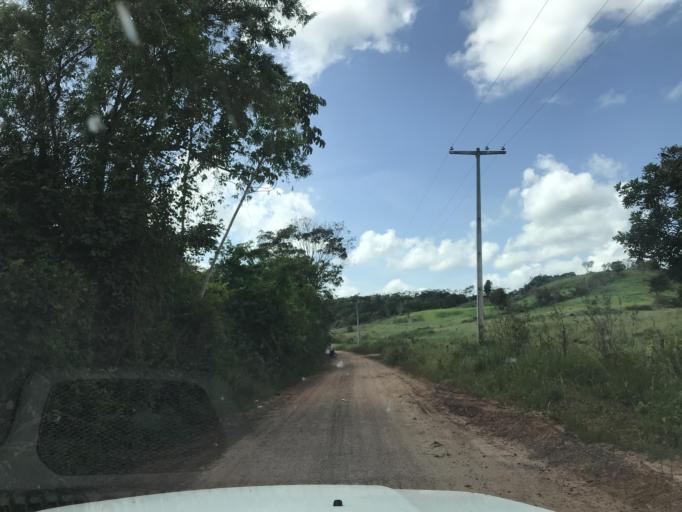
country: BR
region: Bahia
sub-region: Entre Rios
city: Entre Rios
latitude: -12.1741
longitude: -38.0627
